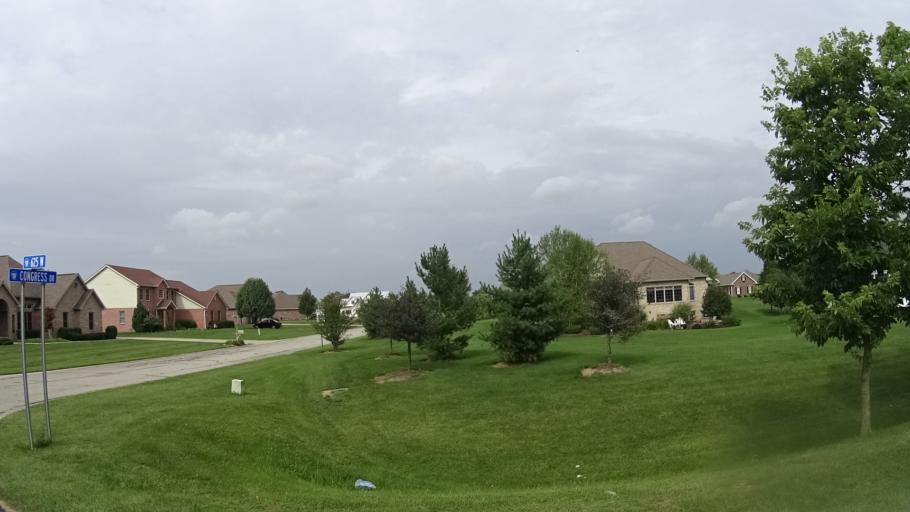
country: US
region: Indiana
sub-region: Madison County
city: Pendleton
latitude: 40.0115
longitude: -85.7912
